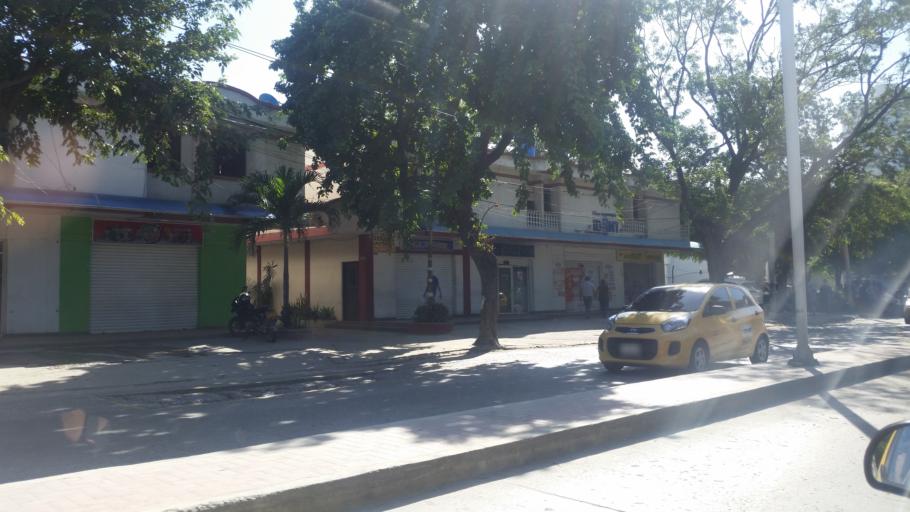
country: CO
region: Magdalena
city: Santa Marta
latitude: 11.2311
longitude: -74.1758
